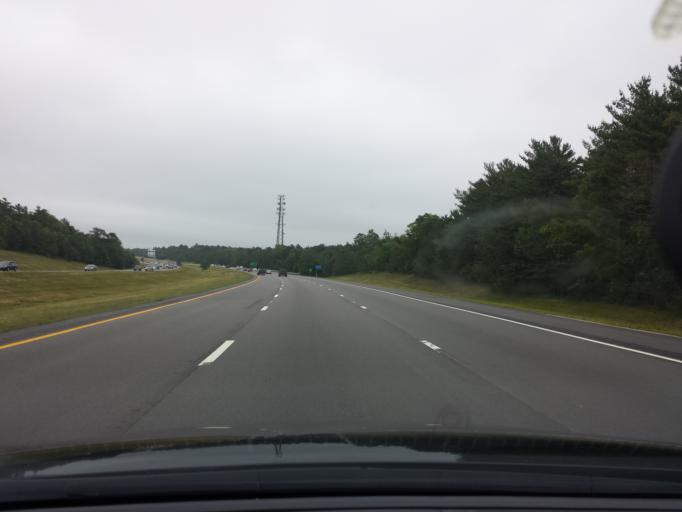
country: US
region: Massachusetts
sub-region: Plymouth County
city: Onset
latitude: 41.7642
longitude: -70.6592
